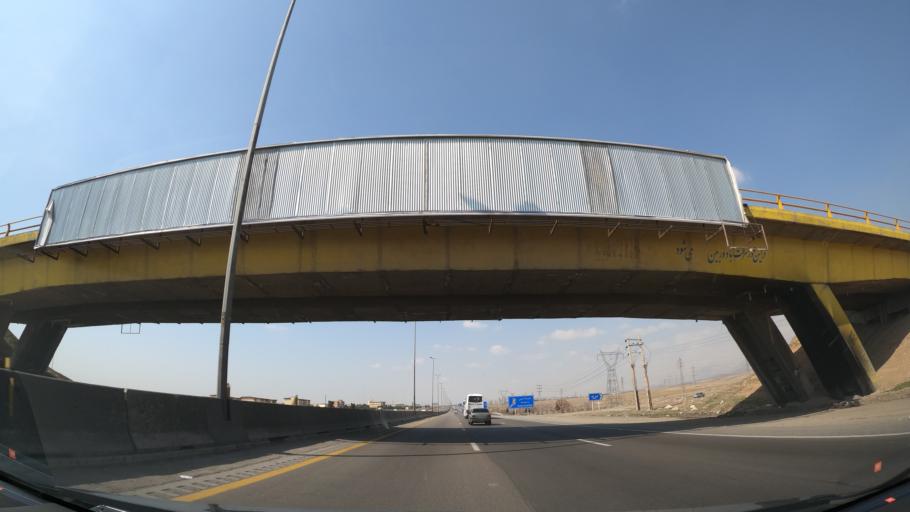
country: IR
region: Qazvin
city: Abyek
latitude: 36.0646
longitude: 50.4901
